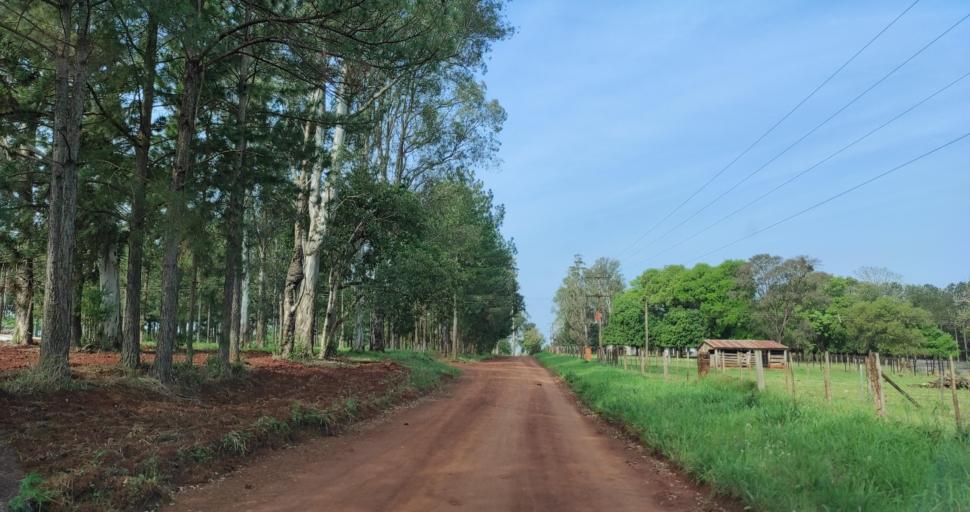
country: AR
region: Misiones
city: Garuhape
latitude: -26.8664
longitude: -54.9969
